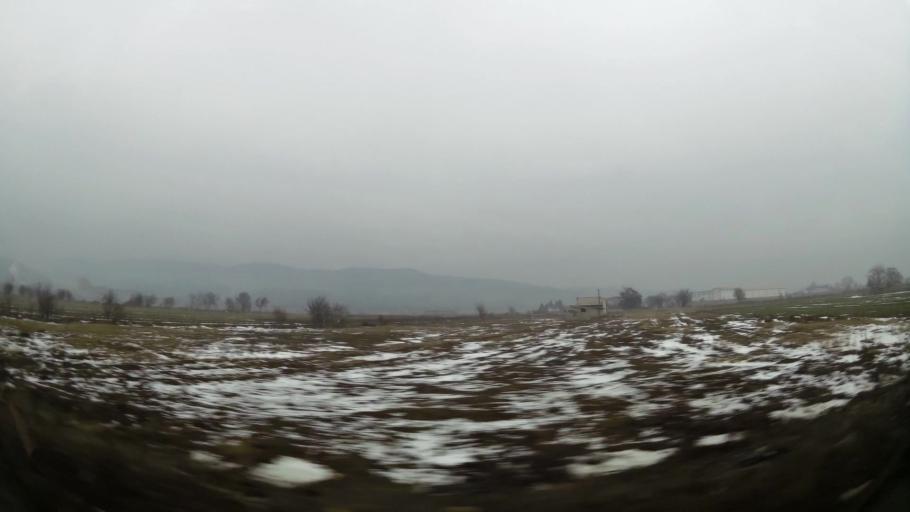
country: MK
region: Cucer-Sandevo
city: Chucher - Sandevo
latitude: 42.0641
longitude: 21.3699
